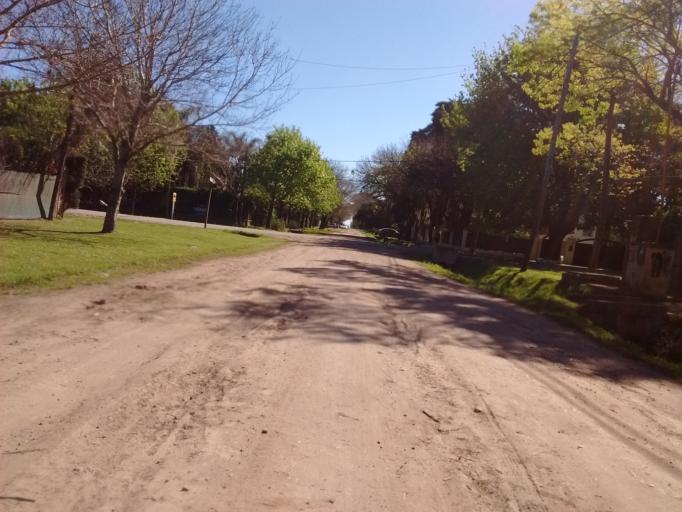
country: AR
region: Santa Fe
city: Funes
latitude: -32.9235
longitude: -60.8162
